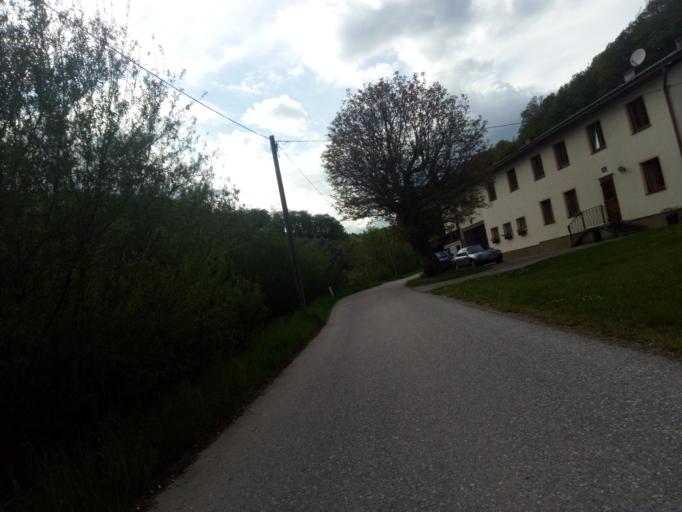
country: AT
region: Lower Austria
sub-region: Politischer Bezirk Wien-Umgebung
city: Wolfsgraben
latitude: 48.1275
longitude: 16.0855
